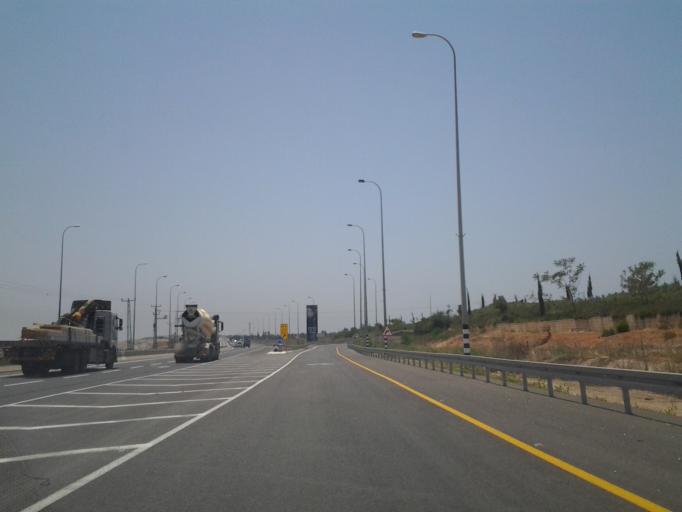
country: IL
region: Haifa
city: Hadera
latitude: 32.4303
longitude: 34.8879
